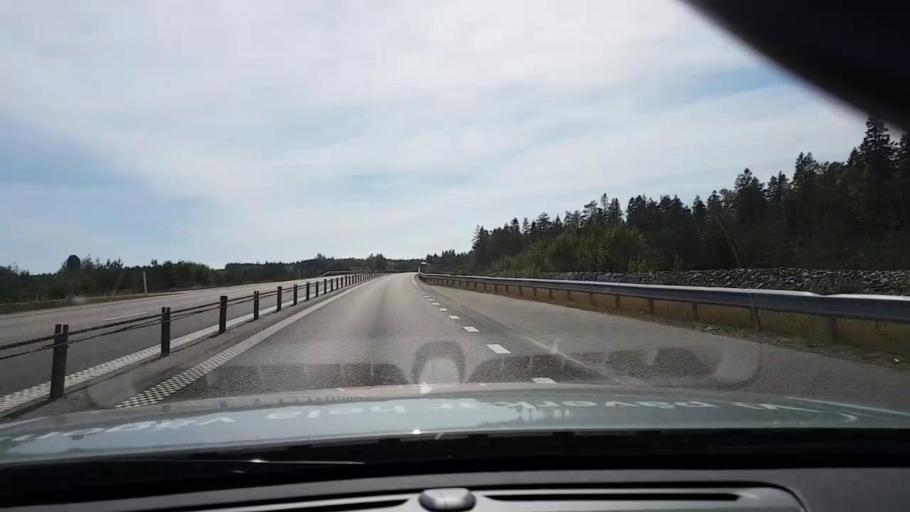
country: SE
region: Vaesternorrland
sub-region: OErnskoeldsviks Kommun
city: Husum
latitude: 63.3700
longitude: 19.1884
